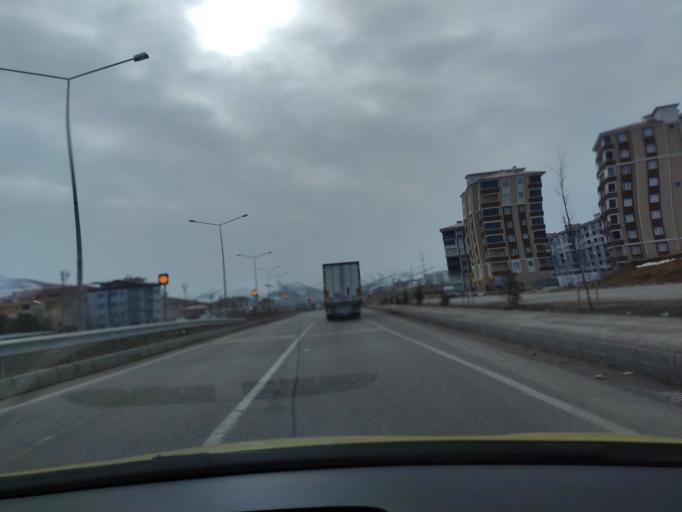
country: TR
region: Bayburt
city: Bayburt
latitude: 40.2663
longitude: 40.2026
